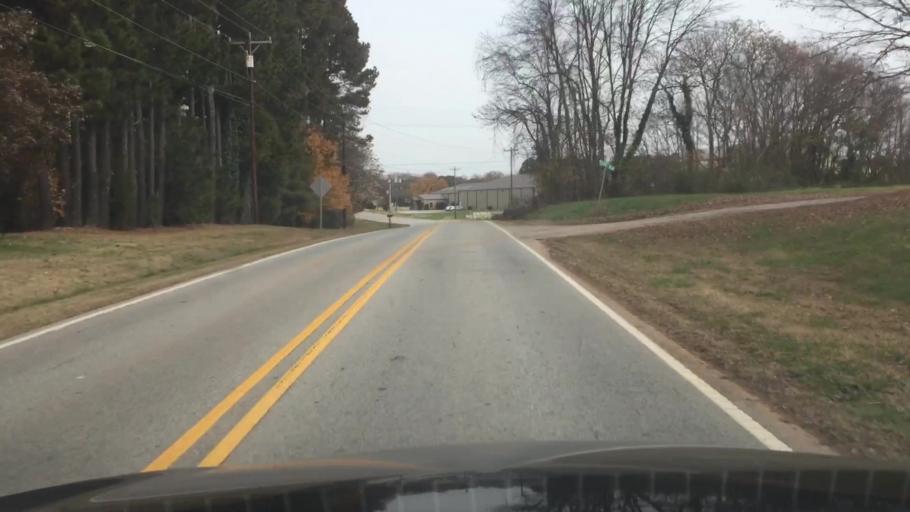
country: US
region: North Carolina
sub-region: Rowan County
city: Enochville
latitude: 35.6232
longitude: -80.6910
